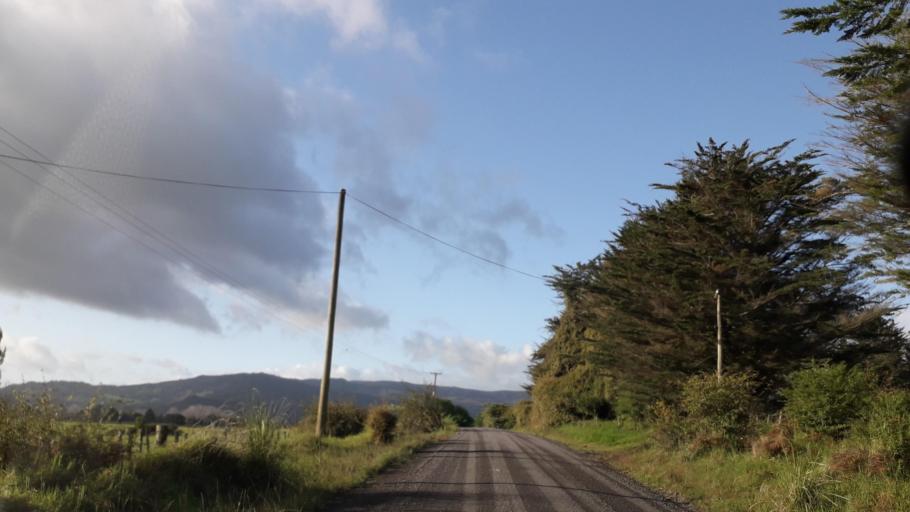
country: NZ
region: Northland
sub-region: Far North District
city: Waimate North
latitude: -35.4926
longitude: 173.6998
